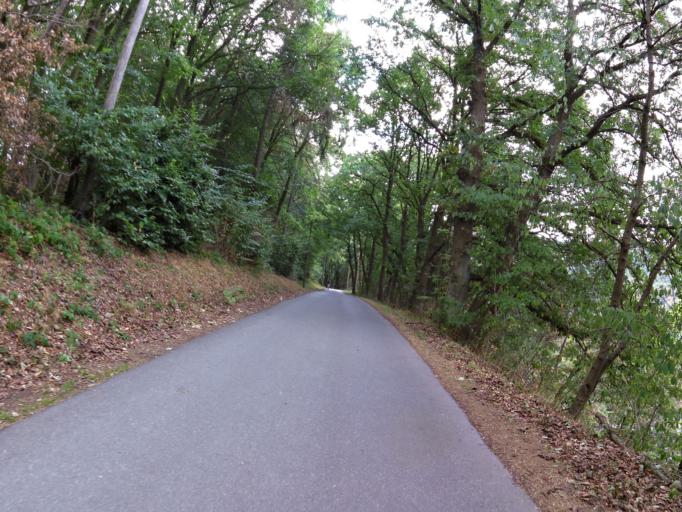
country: DE
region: North Rhine-Westphalia
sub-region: Regierungsbezirk Koln
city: Nideggen
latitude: 50.7104
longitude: 6.4428
